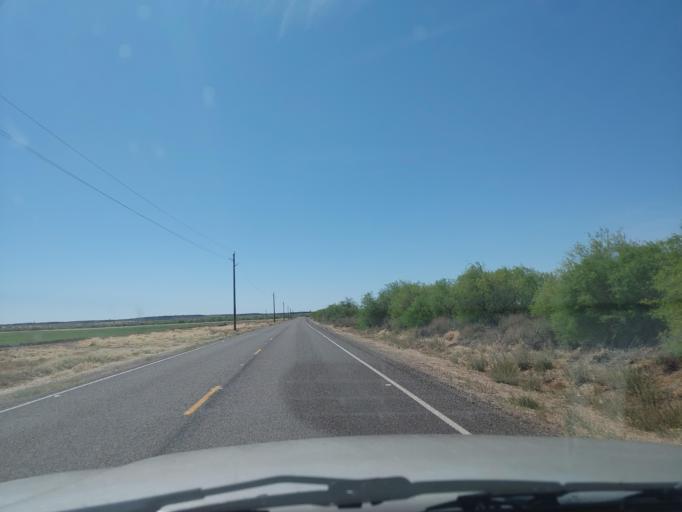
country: US
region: Arizona
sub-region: Maricopa County
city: Gila Bend
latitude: 32.9546
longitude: -113.3056
